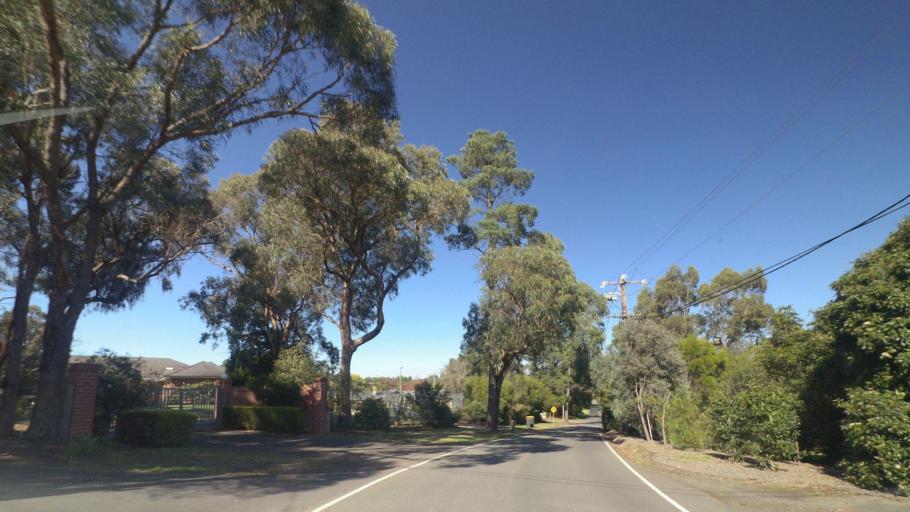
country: AU
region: Victoria
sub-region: Nillumbik
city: Eltham
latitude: -37.7488
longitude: 145.1503
